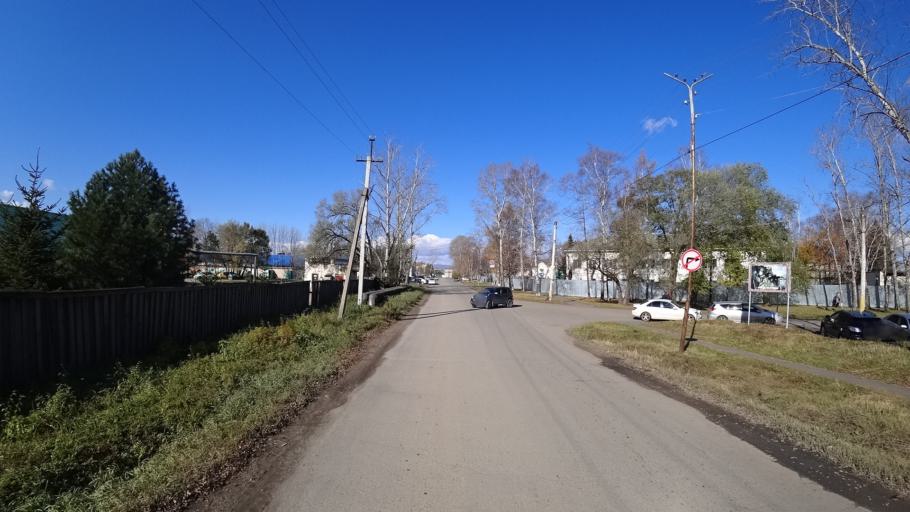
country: RU
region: Khabarovsk Krai
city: Amursk
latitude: 50.0985
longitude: 136.4925
